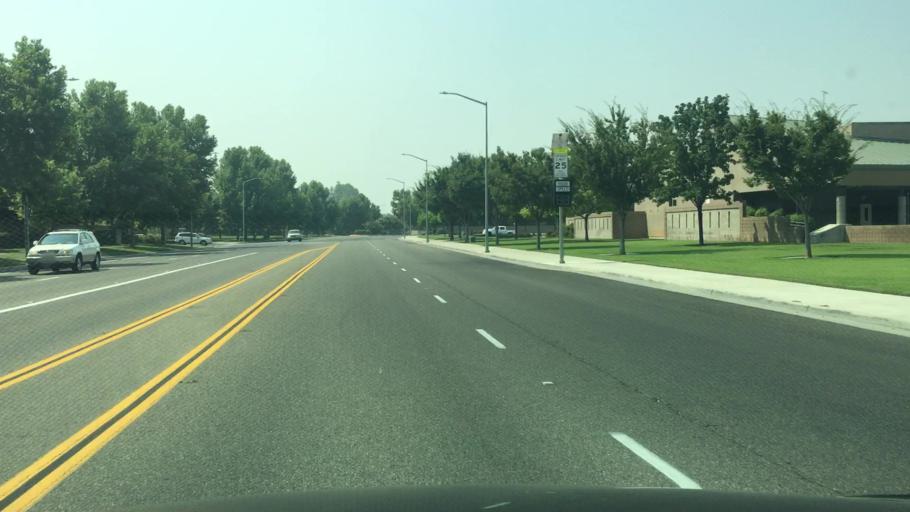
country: US
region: California
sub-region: Fresno County
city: Clovis
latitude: 36.8611
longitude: -119.7022
